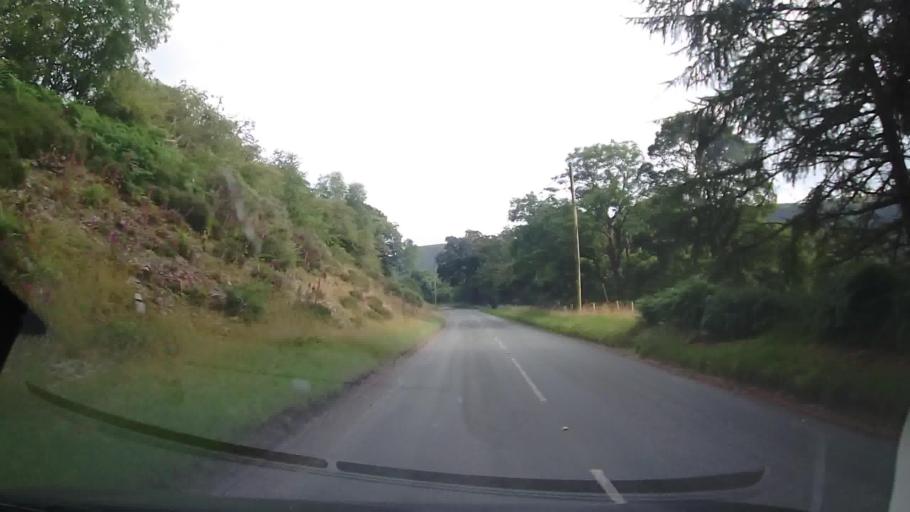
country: GB
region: Wales
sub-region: Sir Powys
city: Llangynog
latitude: 52.8432
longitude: -3.4228
